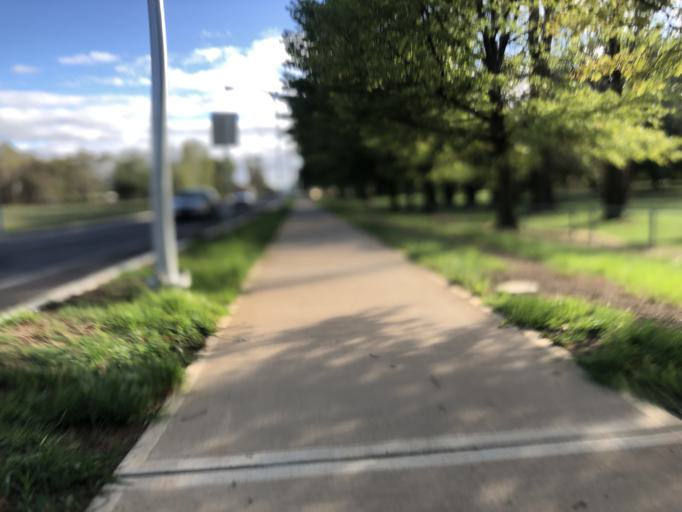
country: AU
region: New South Wales
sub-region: Orange Municipality
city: Orange
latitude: -33.3131
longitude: 149.0939
